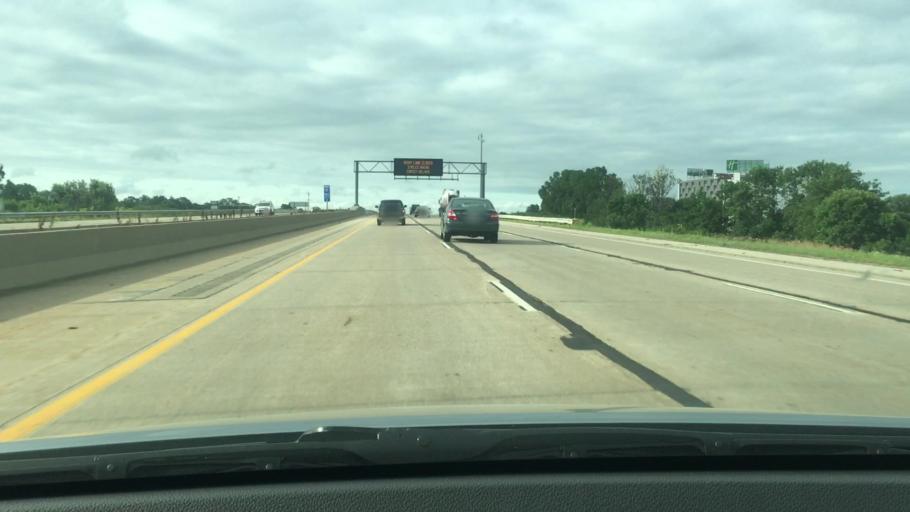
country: US
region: Wisconsin
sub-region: Outagamie County
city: Appleton
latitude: 44.2636
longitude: -88.4664
